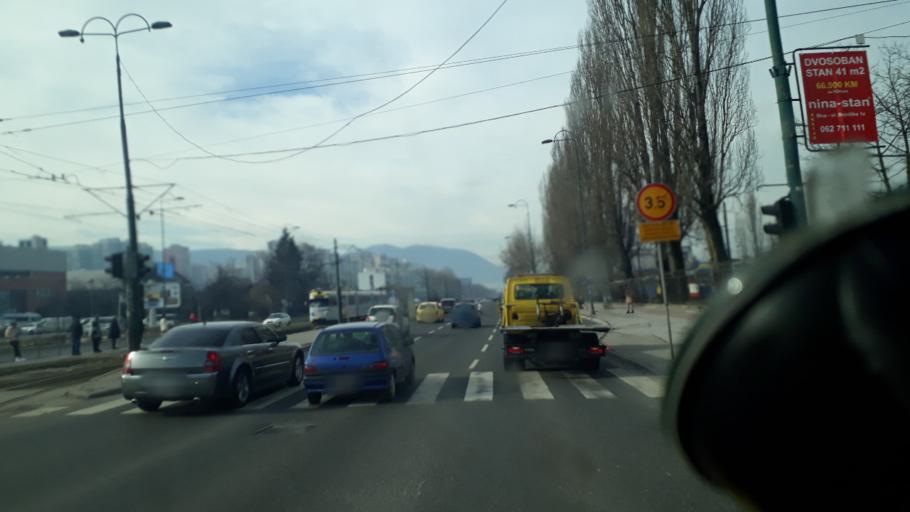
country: BA
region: Federation of Bosnia and Herzegovina
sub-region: Kanton Sarajevo
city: Sarajevo
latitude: 43.8454
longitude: 18.3613
